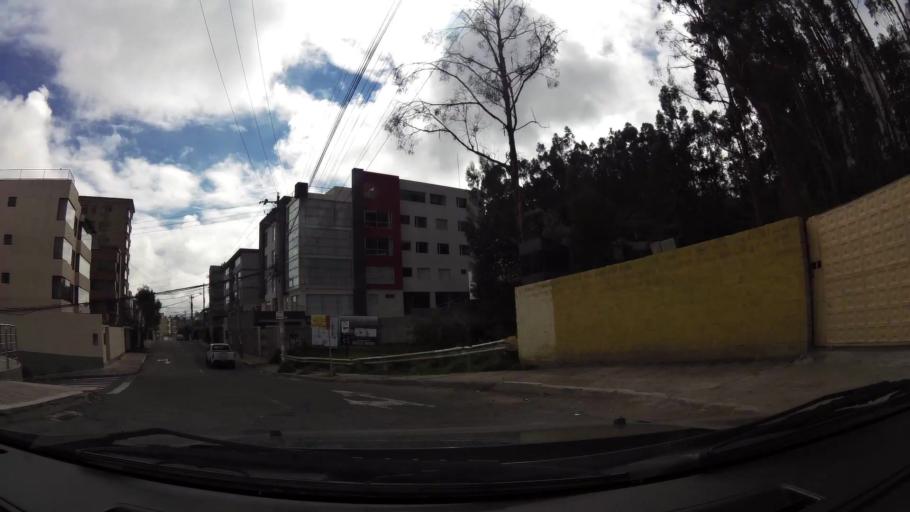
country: EC
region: Pichincha
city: Quito
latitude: -0.1690
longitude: -78.4689
